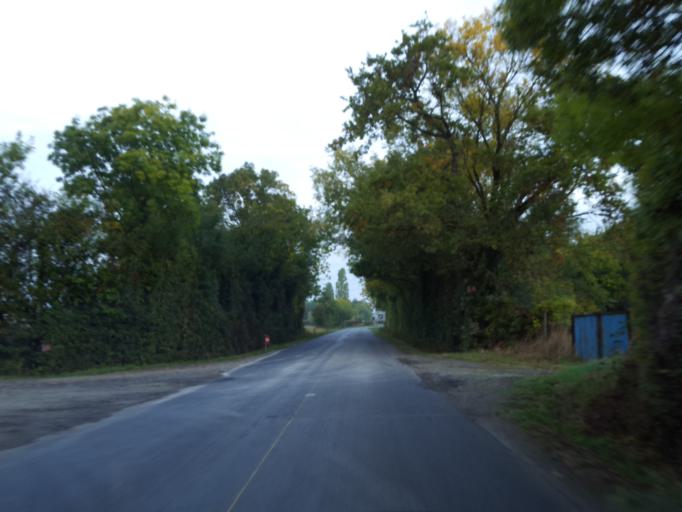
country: FR
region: Pays de la Loire
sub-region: Departement de la Loire-Atlantique
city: Saint-Julien-de-Concelles
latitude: 47.2525
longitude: -1.4073
